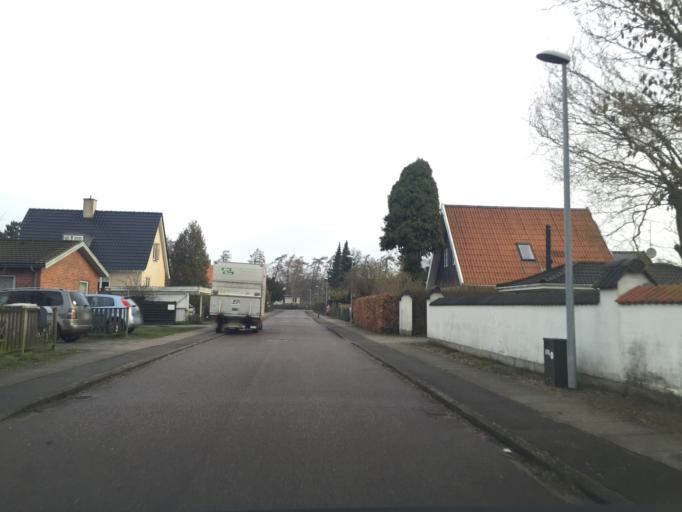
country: DK
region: Capital Region
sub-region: Tarnby Kommune
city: Tarnby
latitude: 55.6257
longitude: 12.6067
